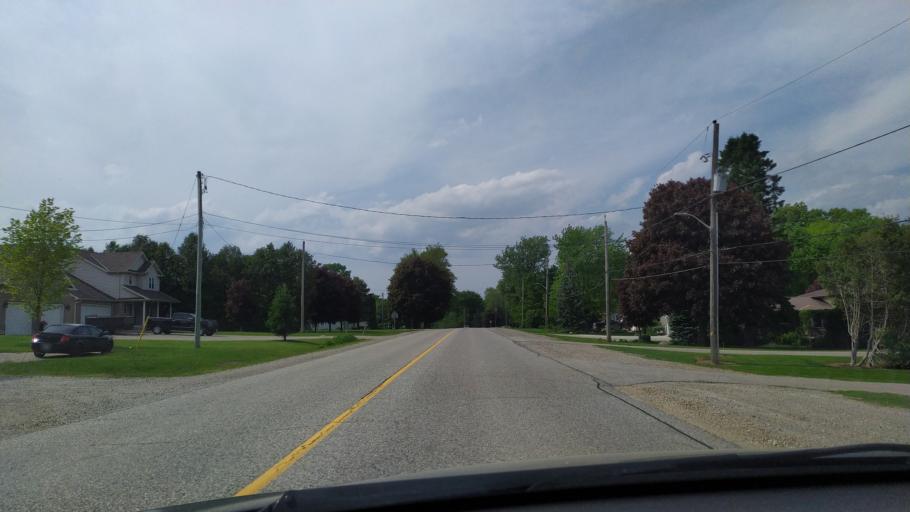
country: CA
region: Ontario
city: Dorchester
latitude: 43.0650
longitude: -81.0001
